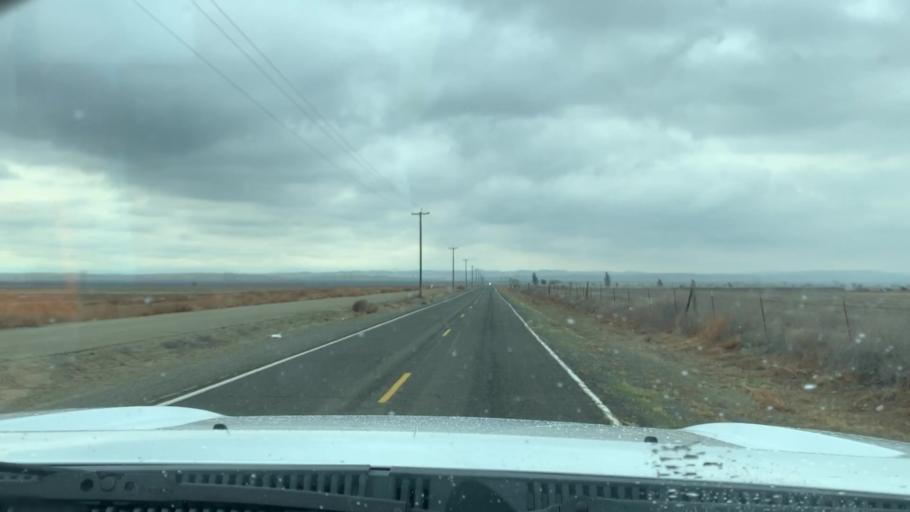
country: US
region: California
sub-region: Kings County
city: Kettleman City
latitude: 35.9342
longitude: -119.8665
